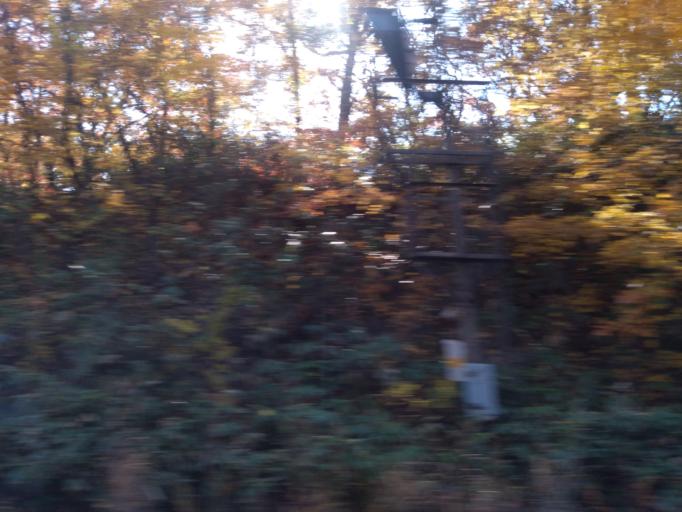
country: JP
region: Hokkaido
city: Kitahiroshima
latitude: 42.9959
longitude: 141.5379
